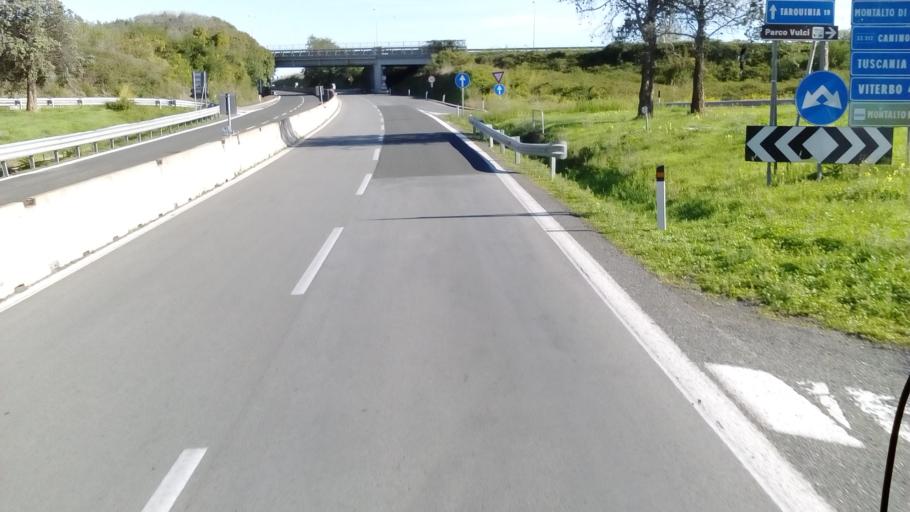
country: IT
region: Latium
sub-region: Provincia di Viterbo
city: Montalto di Castro
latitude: 42.3482
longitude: 11.6029
